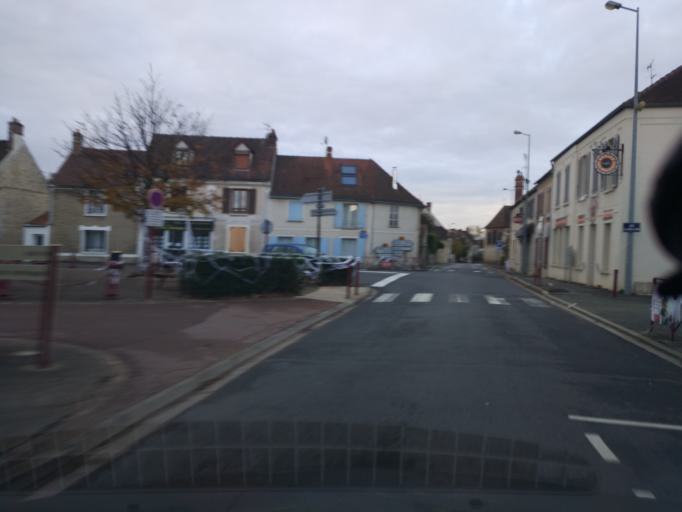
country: FR
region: Ile-de-France
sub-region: Departement de l'Essonne
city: Les Molieres
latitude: 48.6732
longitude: 2.0691
